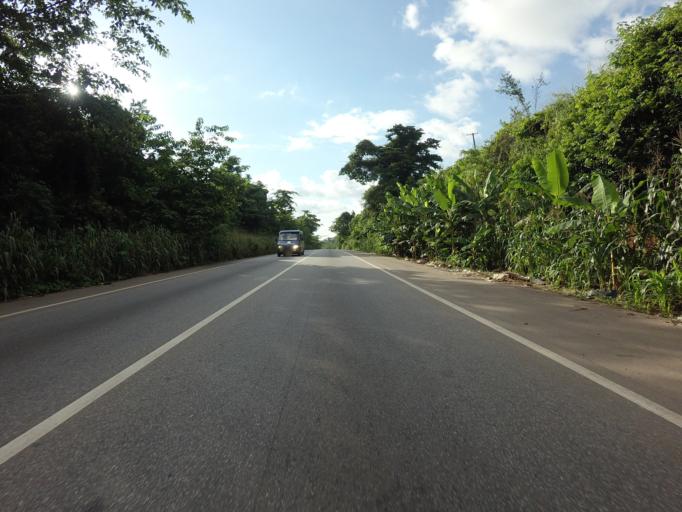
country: GH
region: Ashanti
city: Tafo
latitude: 6.8901
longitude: -1.6481
